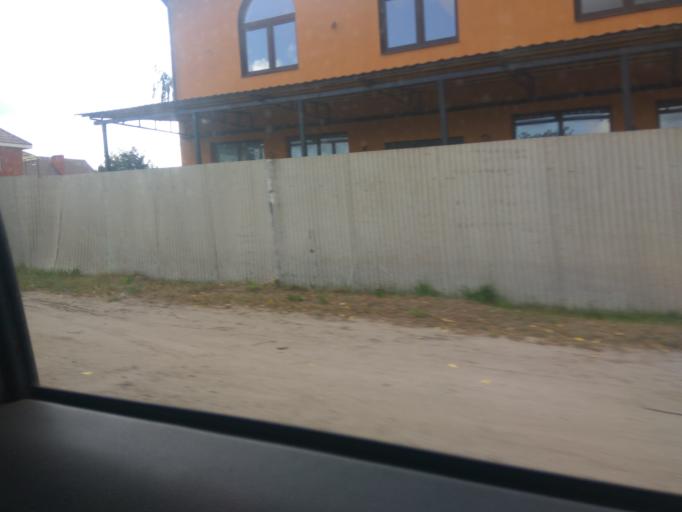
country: RU
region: Moskovskaya
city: Ramenskoye
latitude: 55.5524
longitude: 38.2334
